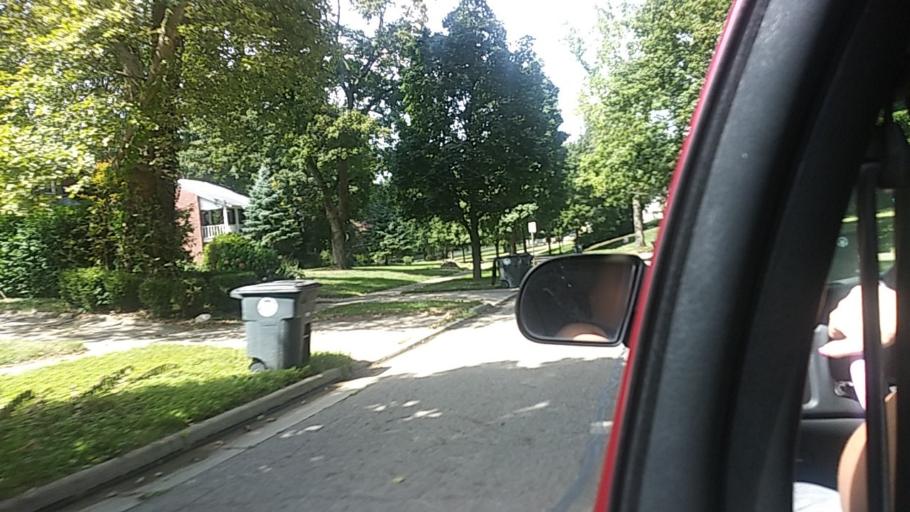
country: US
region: Ohio
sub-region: Summit County
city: Akron
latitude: 41.0951
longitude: -81.5578
